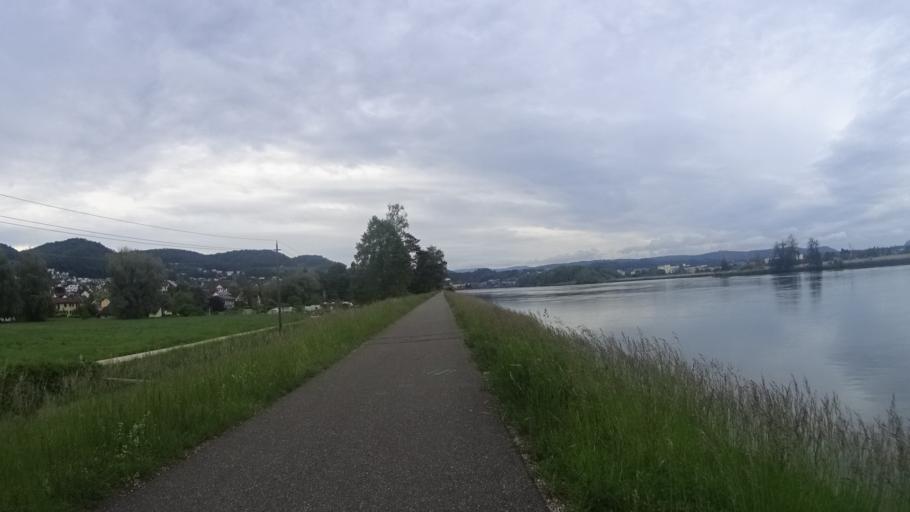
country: CH
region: Aargau
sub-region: Bezirk Zurzach
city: Klingnau
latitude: 47.5824
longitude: 8.2417
